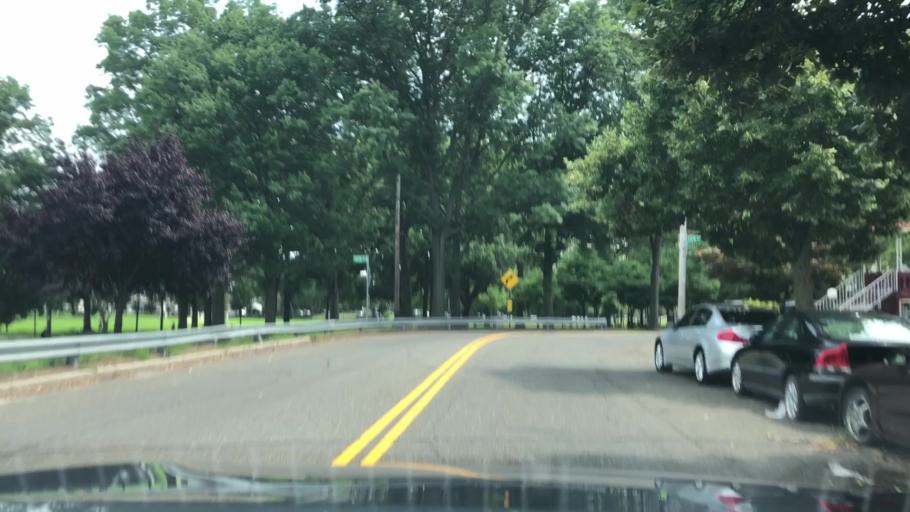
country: US
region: New York
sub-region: Queens County
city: Jamaica
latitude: 40.6755
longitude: -73.7869
